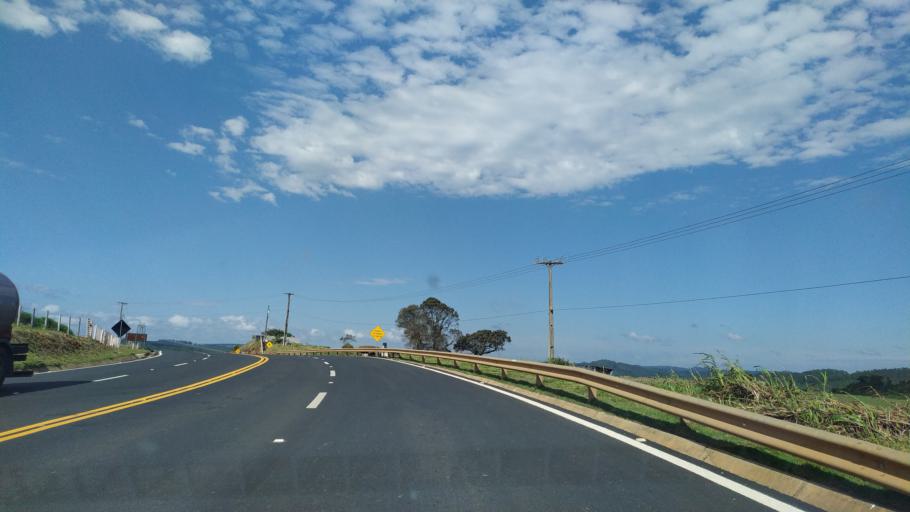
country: BR
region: Parana
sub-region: Telemaco Borba
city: Telemaco Borba
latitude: -24.2811
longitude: -50.7140
